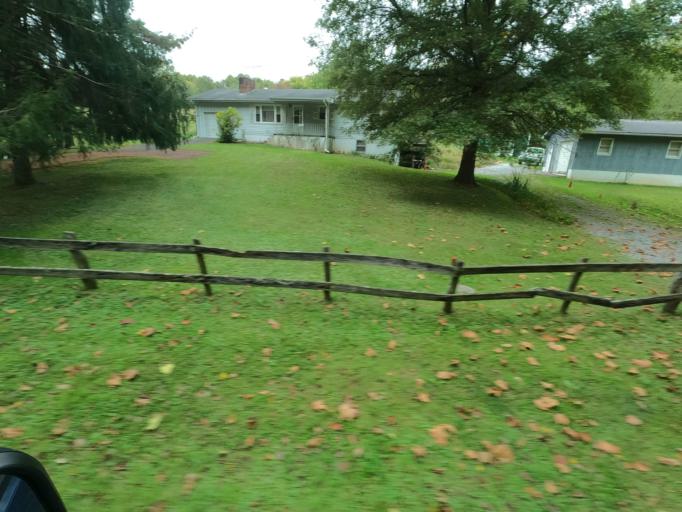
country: US
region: Tennessee
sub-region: Washington County
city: Jonesborough
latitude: 36.2680
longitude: -82.5360
